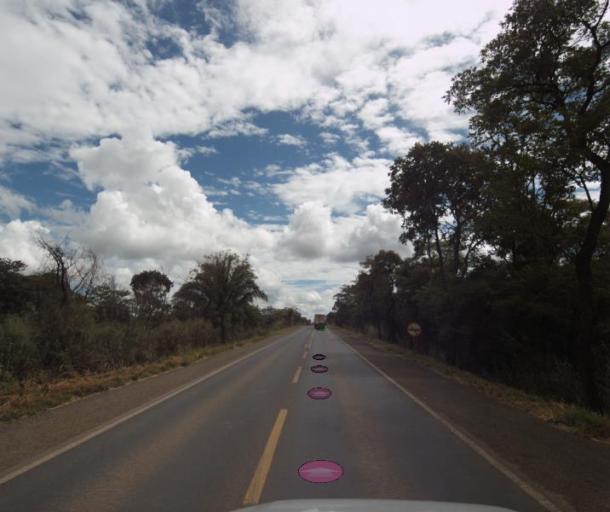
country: BR
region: Goias
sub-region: Uruacu
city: Uruacu
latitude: -14.4519
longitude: -49.1564
